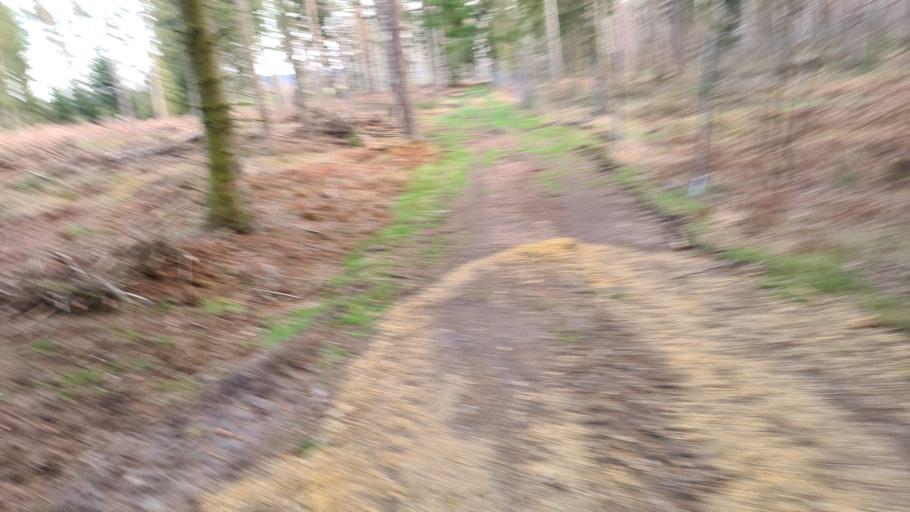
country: DE
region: Brandenburg
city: Schonborn
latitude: 51.5625
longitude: 13.4657
